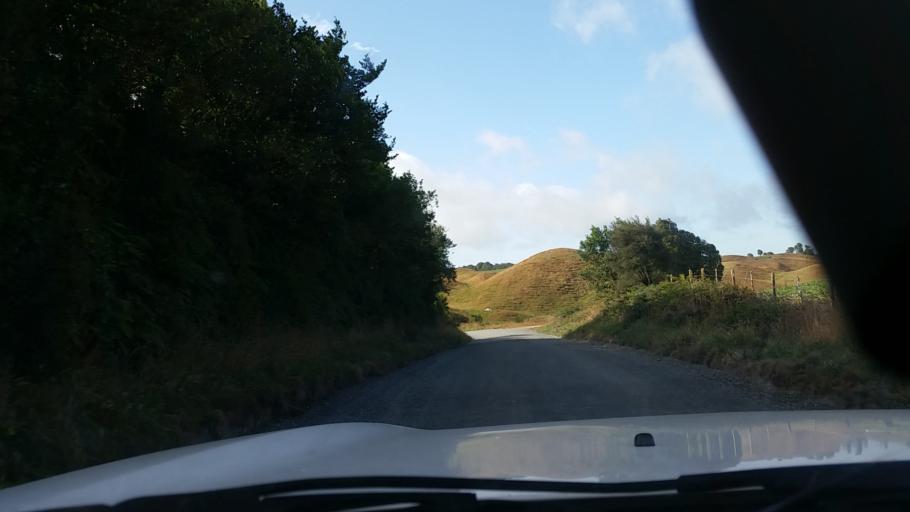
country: NZ
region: Bay of Plenty
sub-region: Rotorua District
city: Rotorua
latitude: -38.1382
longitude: 176.0794
